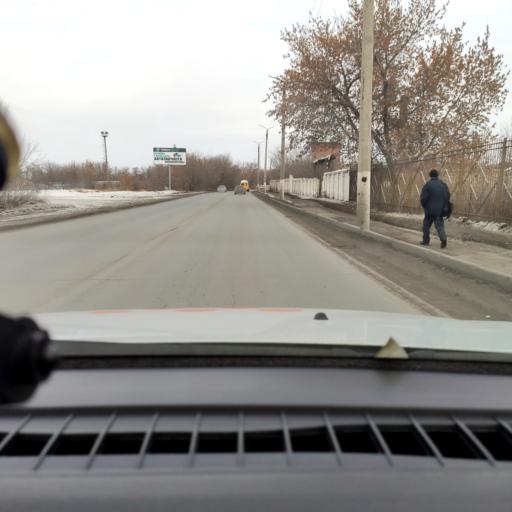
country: RU
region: Samara
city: Chapayevsk
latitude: 52.9665
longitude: 49.6940
